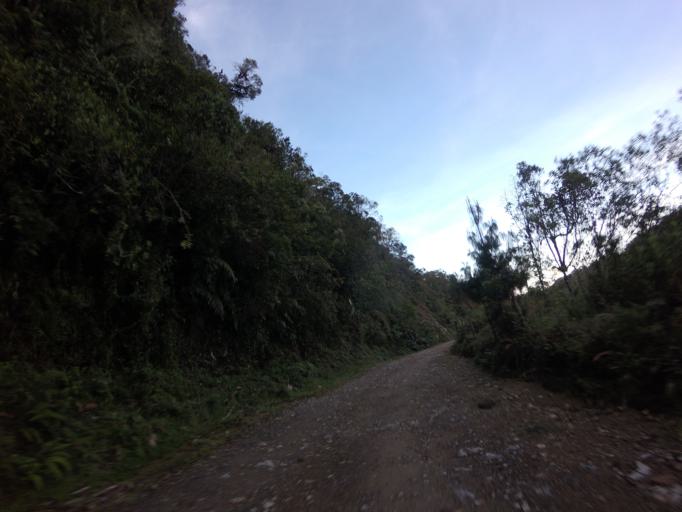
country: CO
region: Caldas
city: Pensilvania
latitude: 5.4373
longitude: -75.1322
